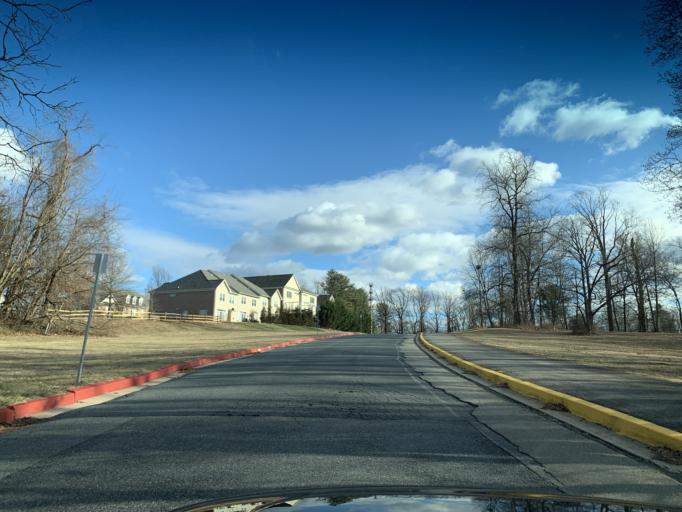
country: US
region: Maryland
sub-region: Harford County
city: South Bel Air
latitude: 39.5270
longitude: -76.3420
